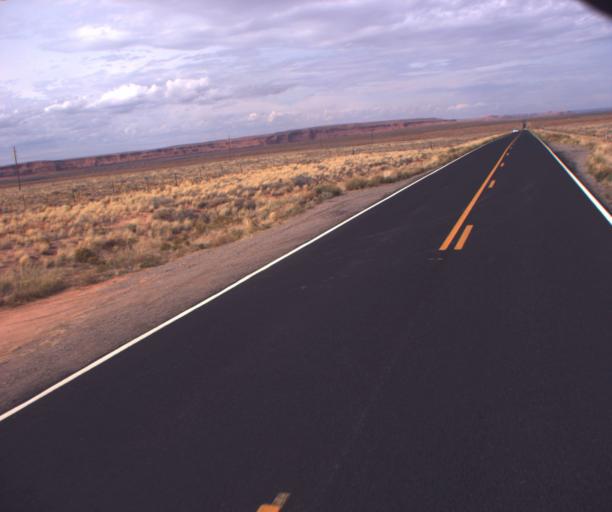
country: US
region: Arizona
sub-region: Apache County
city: Many Farms
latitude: 36.5686
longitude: -109.5459
